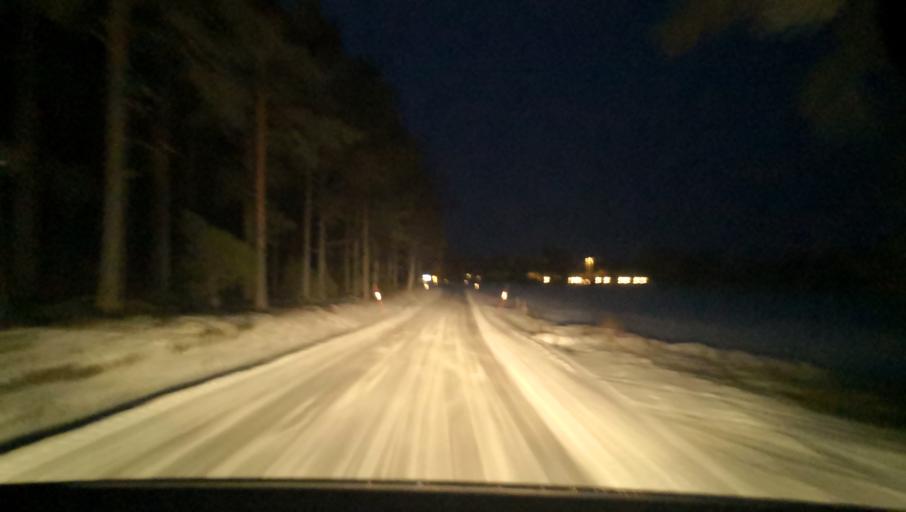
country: SE
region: Uppsala
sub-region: Heby Kommun
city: Tarnsjo
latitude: 60.2956
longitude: 16.8047
